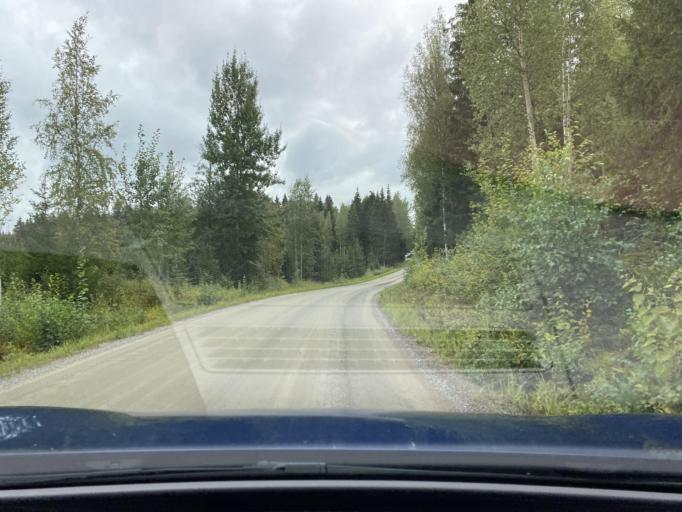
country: FI
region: Pirkanmaa
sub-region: Lounais-Pirkanmaa
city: Punkalaidun
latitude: 61.2196
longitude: 23.1650
